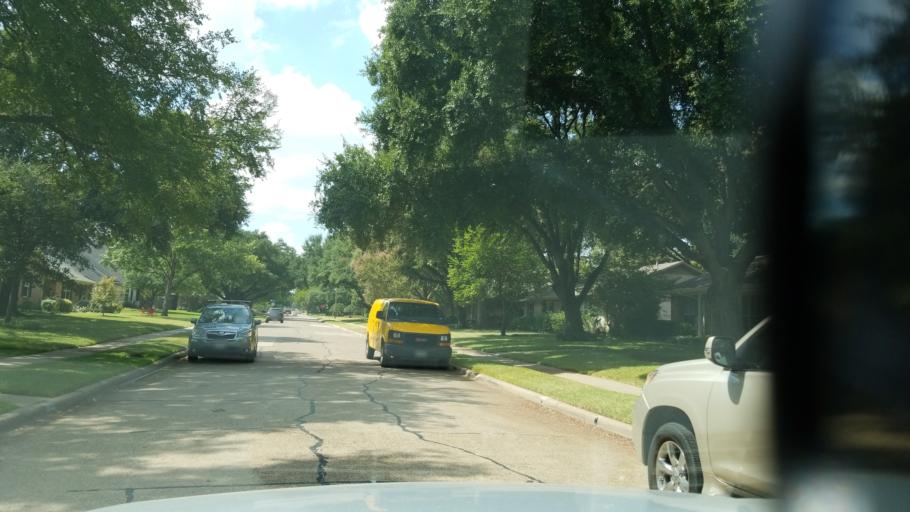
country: US
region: Texas
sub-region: Dallas County
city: Richardson
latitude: 32.9690
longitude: -96.7589
